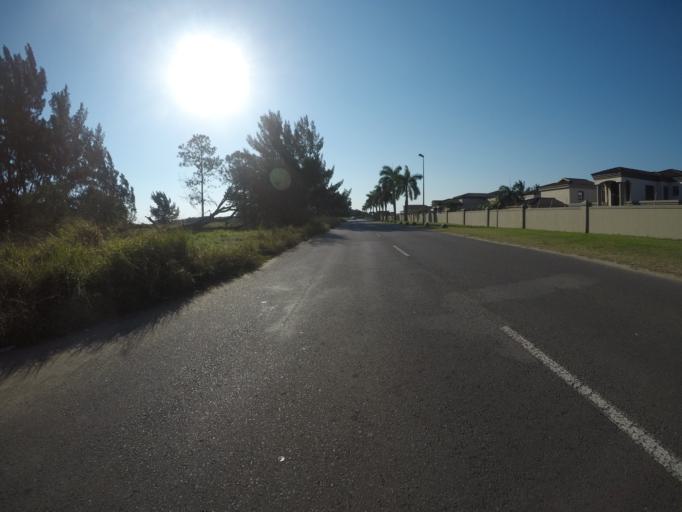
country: ZA
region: KwaZulu-Natal
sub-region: uThungulu District Municipality
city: Richards Bay
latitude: -28.7902
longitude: 32.0807
